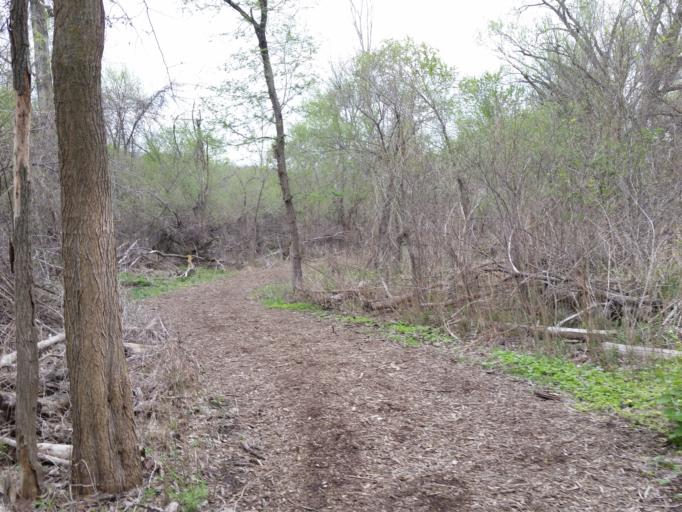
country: US
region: Nebraska
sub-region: Sarpy County
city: Bellevue
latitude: 41.1473
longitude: -95.8847
